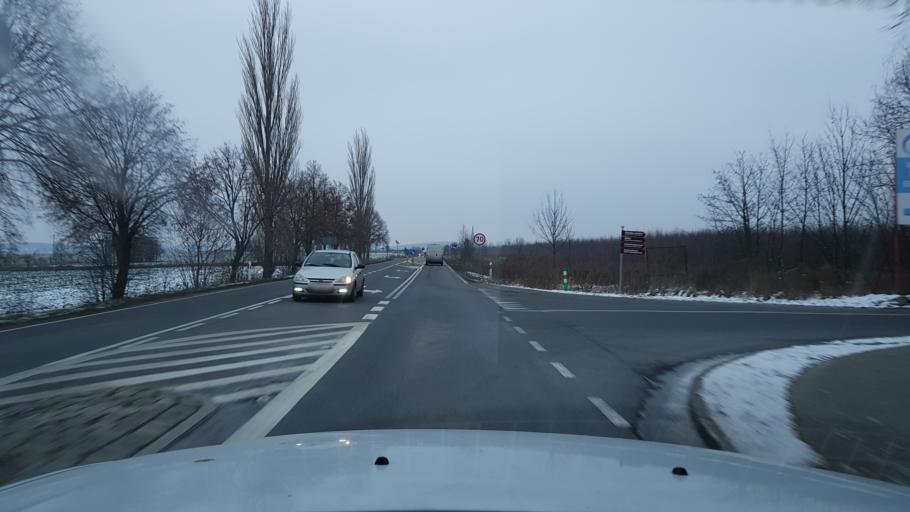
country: PL
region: West Pomeranian Voivodeship
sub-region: Powiat gryfinski
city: Chojna
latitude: 52.9526
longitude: 14.4079
